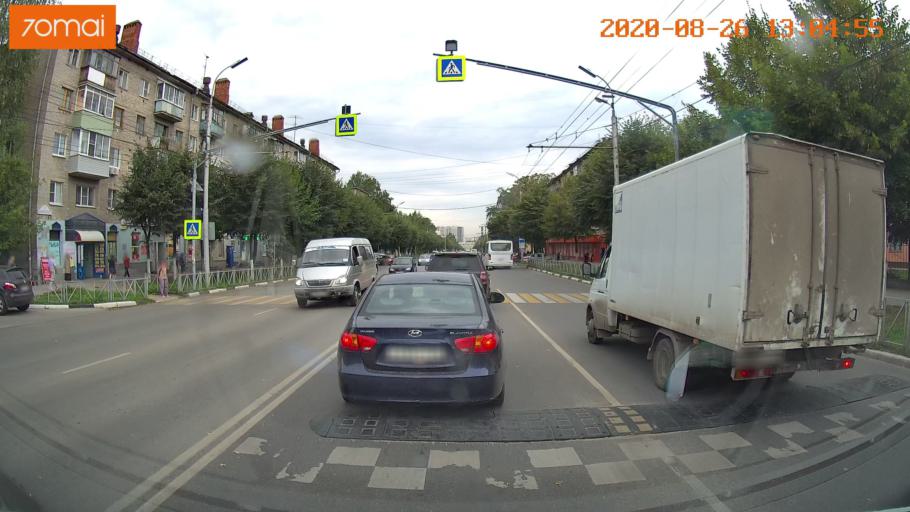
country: RU
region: Rjazan
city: Ryazan'
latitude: 54.6181
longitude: 39.7278
